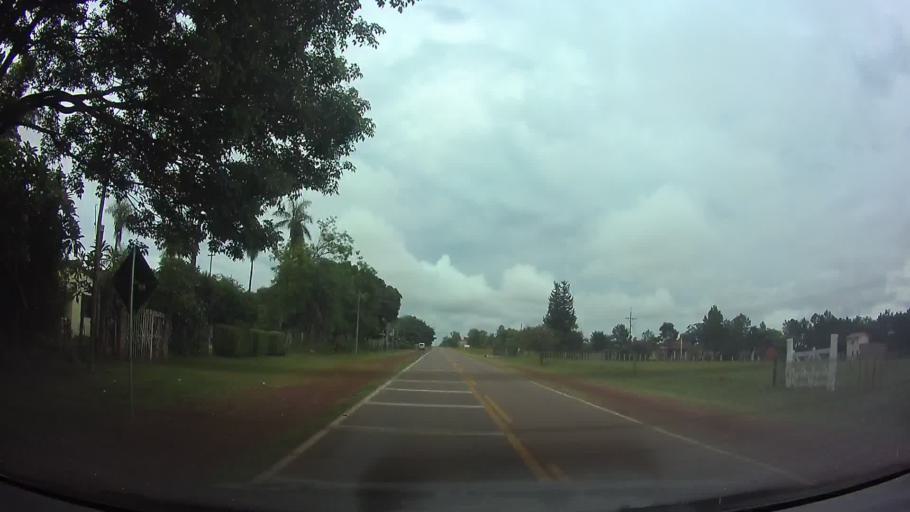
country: PY
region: Paraguari
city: Carapegua
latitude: -25.7985
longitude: -57.1951
